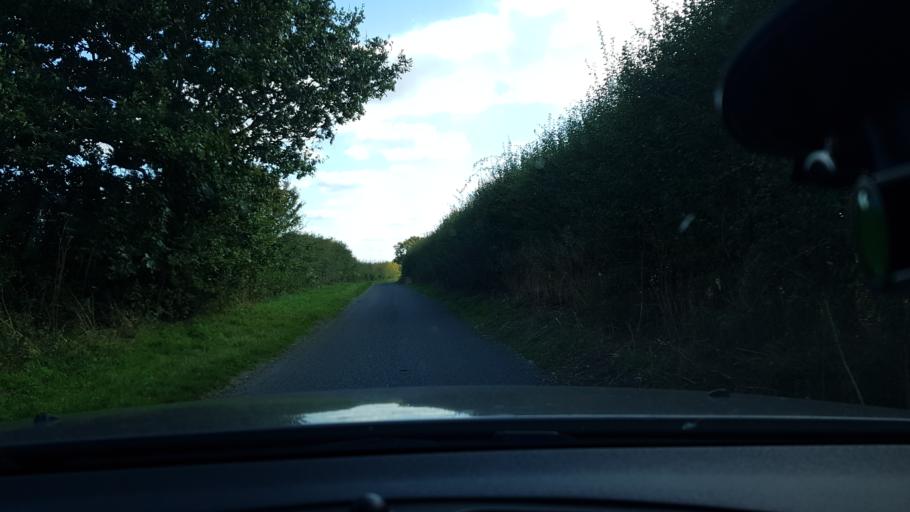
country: GB
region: England
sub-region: West Berkshire
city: Wickham
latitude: 51.4254
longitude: -1.4492
